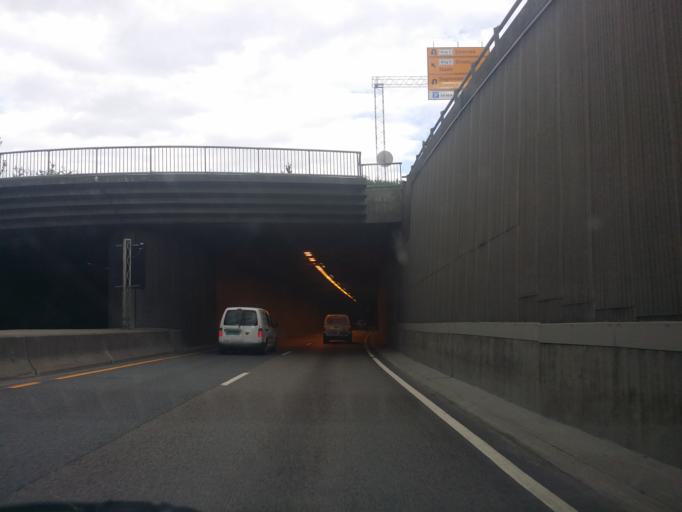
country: NO
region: Oslo
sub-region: Oslo
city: Oslo
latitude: 59.9511
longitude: 10.7389
